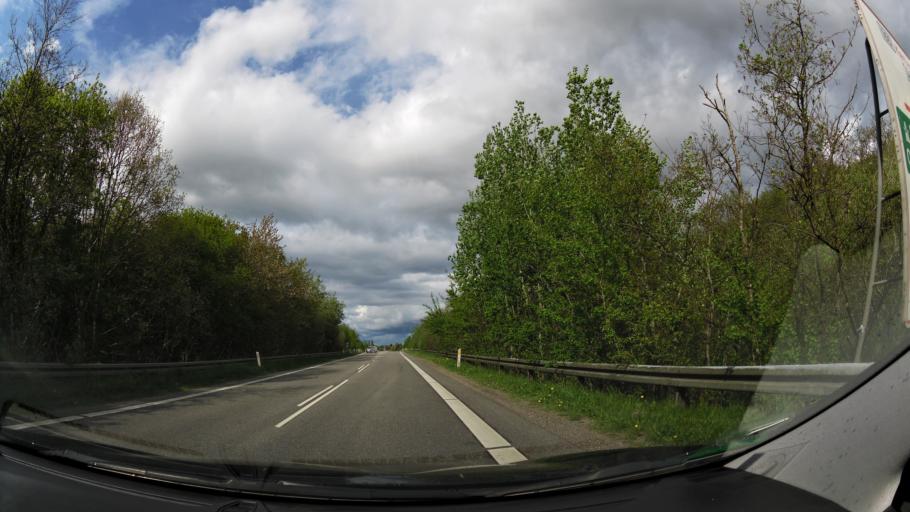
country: DK
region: South Denmark
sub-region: Nyborg Kommune
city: Nyborg
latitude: 55.3296
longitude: 10.7403
